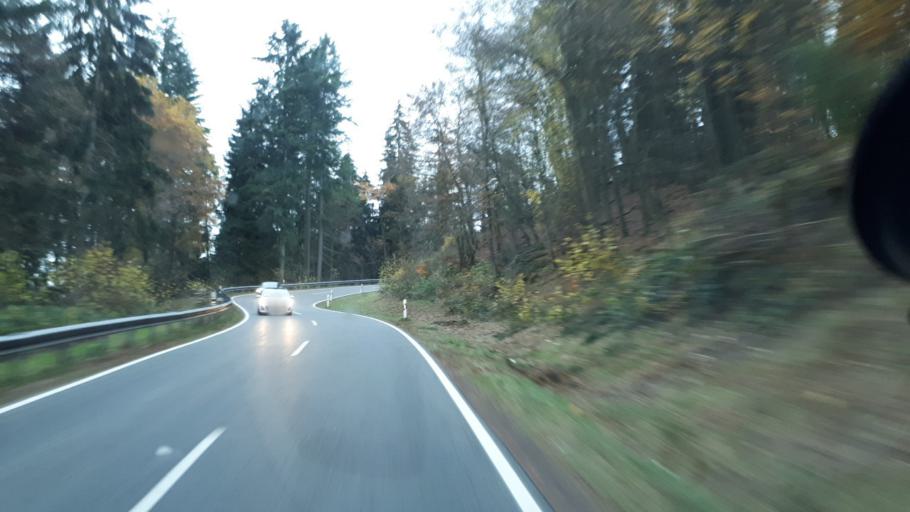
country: DE
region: Rheinland-Pfalz
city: Leienkaul
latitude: 50.1990
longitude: 7.0923
